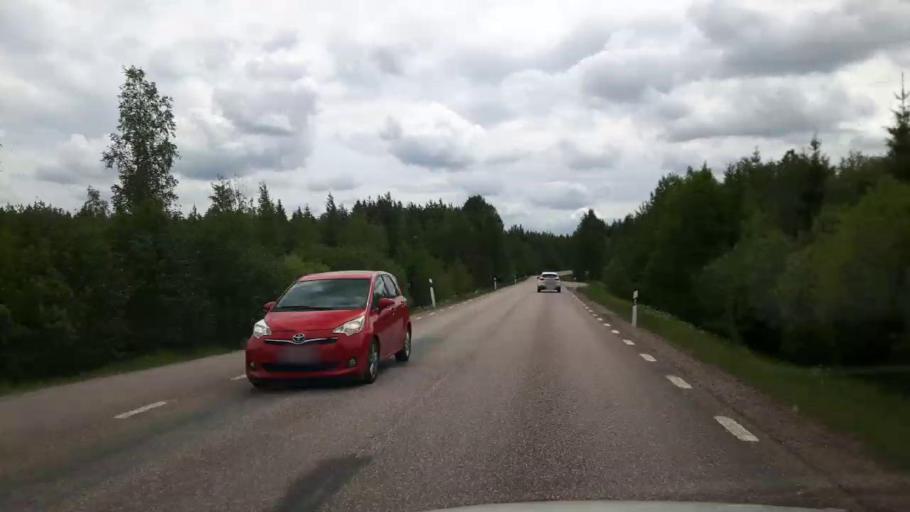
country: SE
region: Vaestmanland
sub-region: Norbergs Kommun
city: Norberg
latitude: 60.1242
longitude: 15.9185
